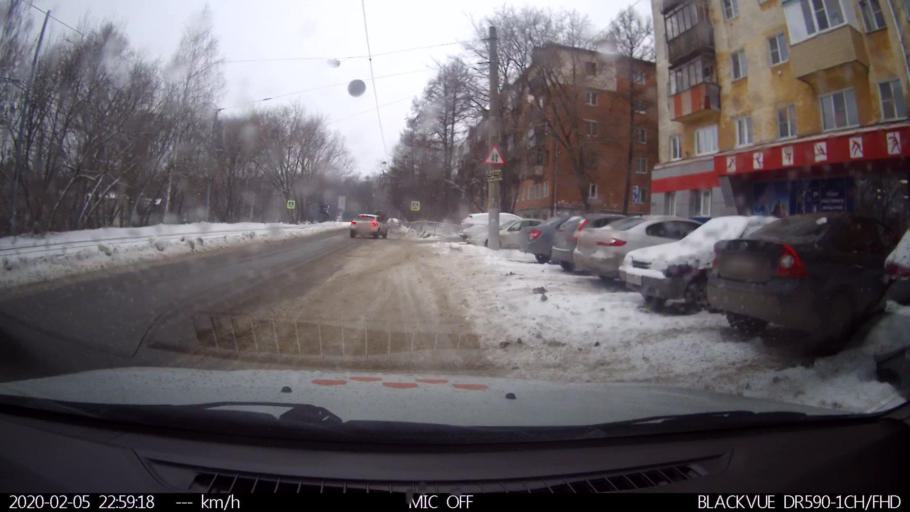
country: RU
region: Penza
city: Bogoslovka
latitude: 53.2065
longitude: 44.8645
